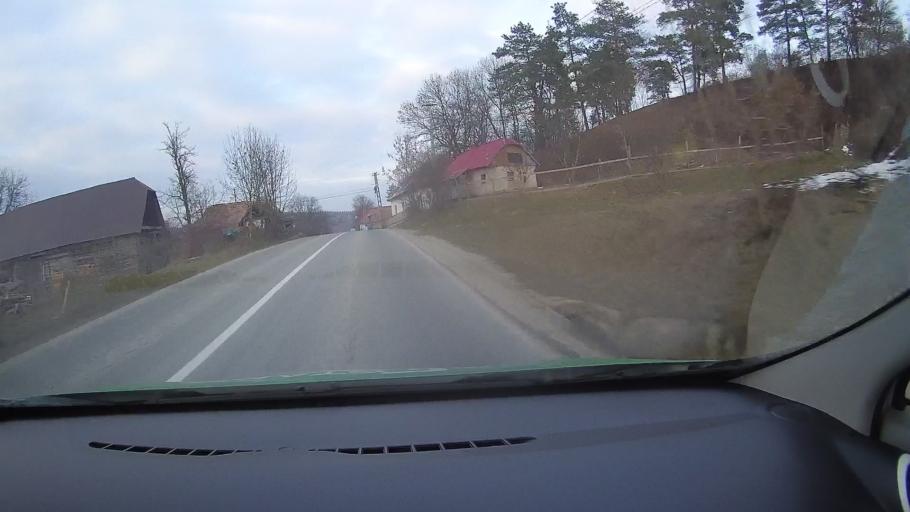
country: RO
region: Harghita
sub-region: Comuna Simonesti
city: Simonesti
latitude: 46.3523
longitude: 25.1318
